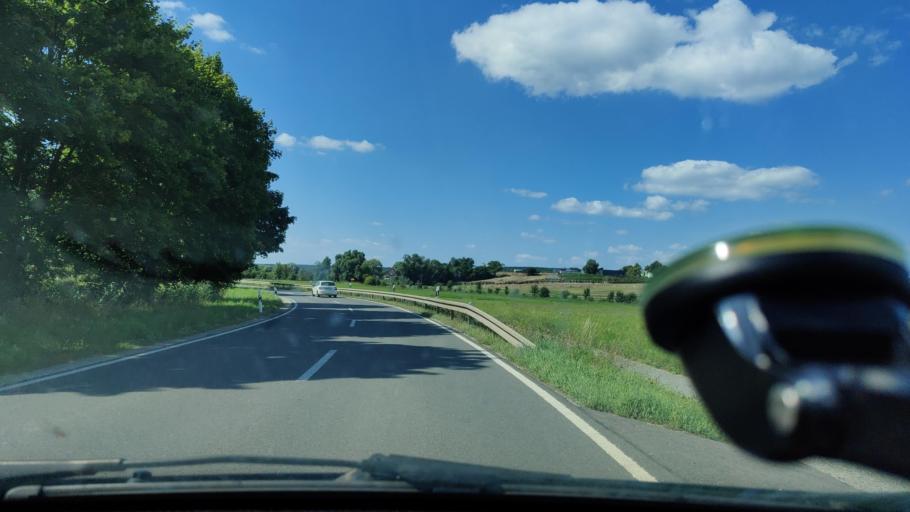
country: DE
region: Thuringia
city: Blankenhain
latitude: 50.8539
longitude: 11.3567
